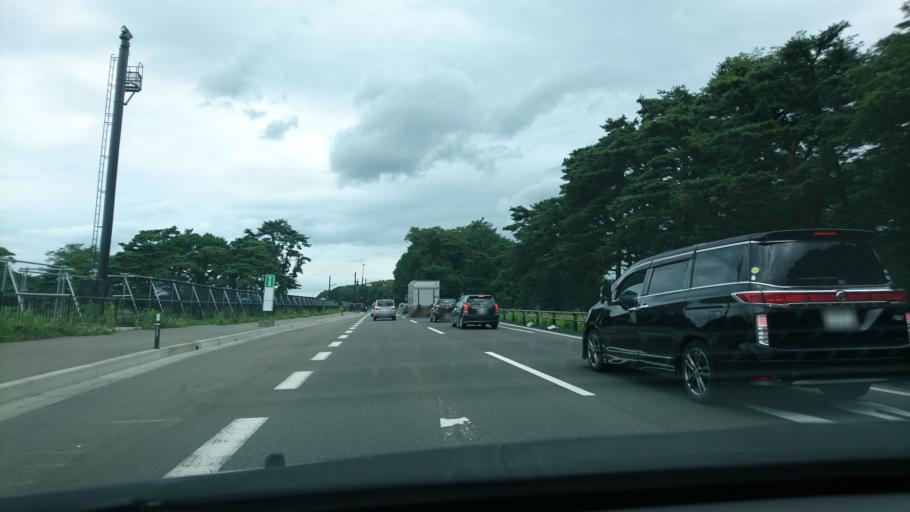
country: JP
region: Iwate
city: Morioka-shi
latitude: 39.7819
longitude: 141.1252
